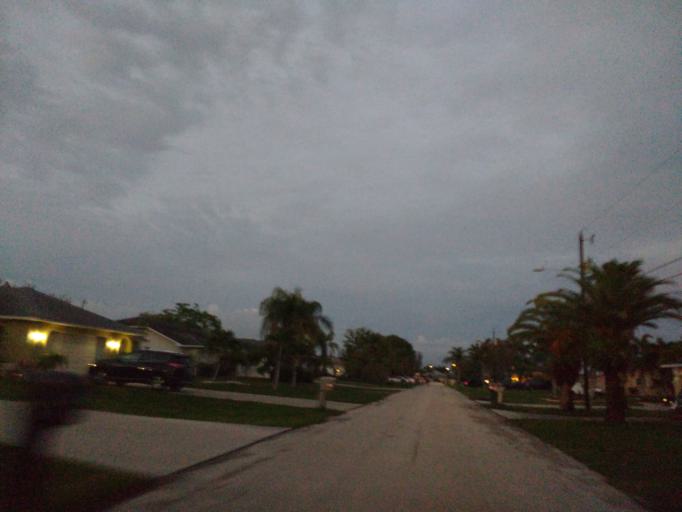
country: US
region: Florida
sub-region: Lee County
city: Cape Coral
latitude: 26.6151
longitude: -81.9667
